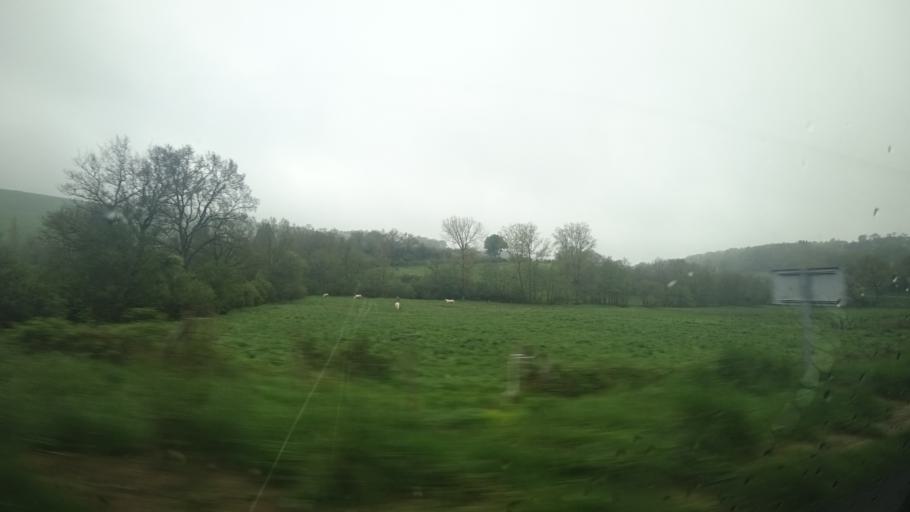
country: FR
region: Midi-Pyrenees
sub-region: Departement de l'Aveyron
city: Laissac
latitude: 44.2683
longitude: 2.9064
